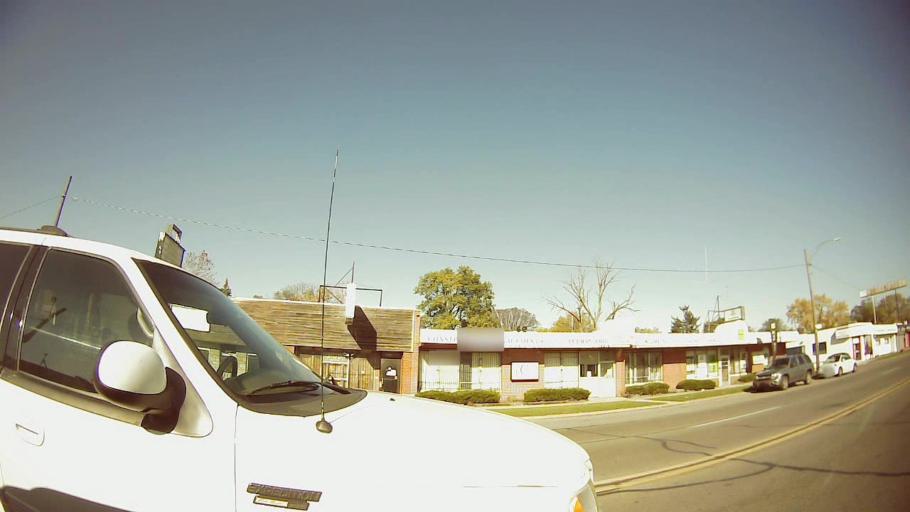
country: US
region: Michigan
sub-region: Oakland County
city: Oak Park
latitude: 42.4303
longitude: -83.2078
